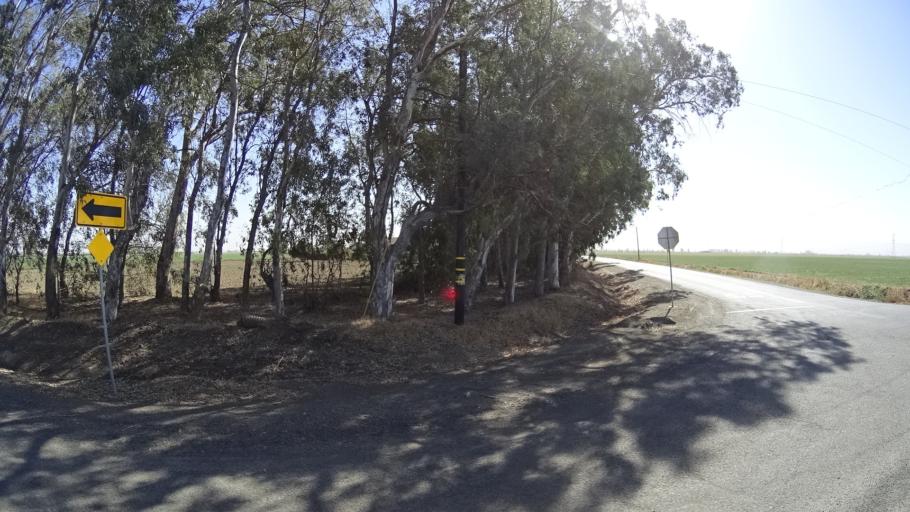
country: US
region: California
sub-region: Yolo County
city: Winters
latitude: 38.5836
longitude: -121.9059
